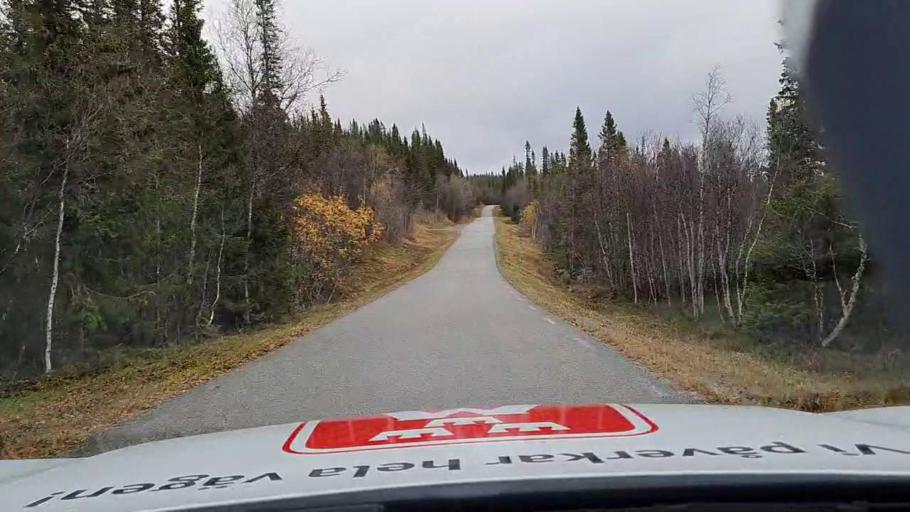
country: SE
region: Jaemtland
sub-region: Bergs Kommun
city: Hoverberg
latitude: 63.0117
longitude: 13.9421
